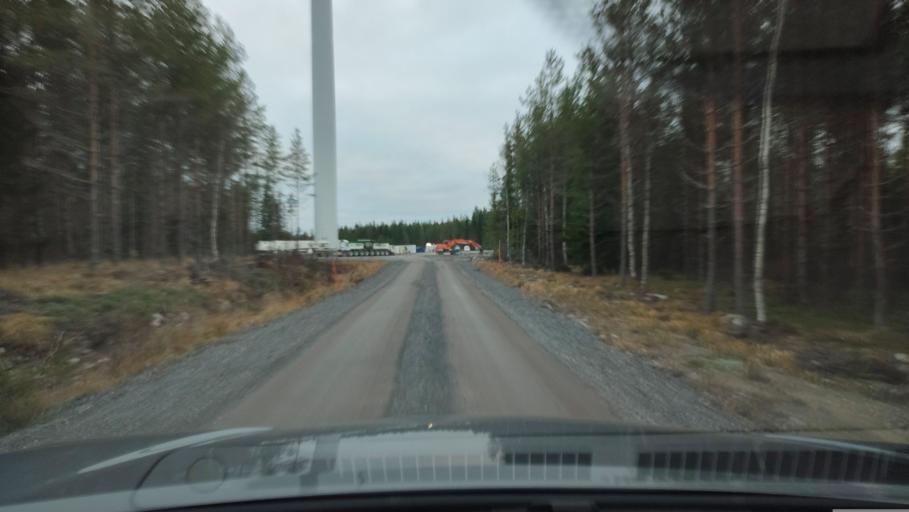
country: FI
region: Southern Ostrobothnia
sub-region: Suupohja
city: Karijoki
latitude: 62.1868
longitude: 21.5632
